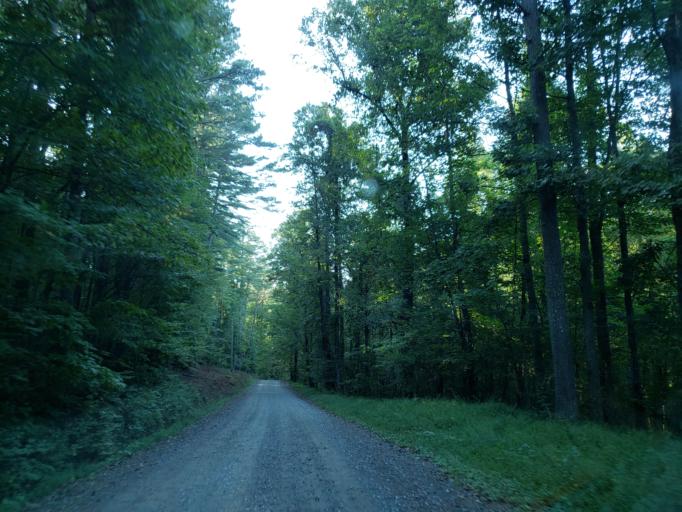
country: US
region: Georgia
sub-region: Fannin County
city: Blue Ridge
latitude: 34.6833
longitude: -84.2651
